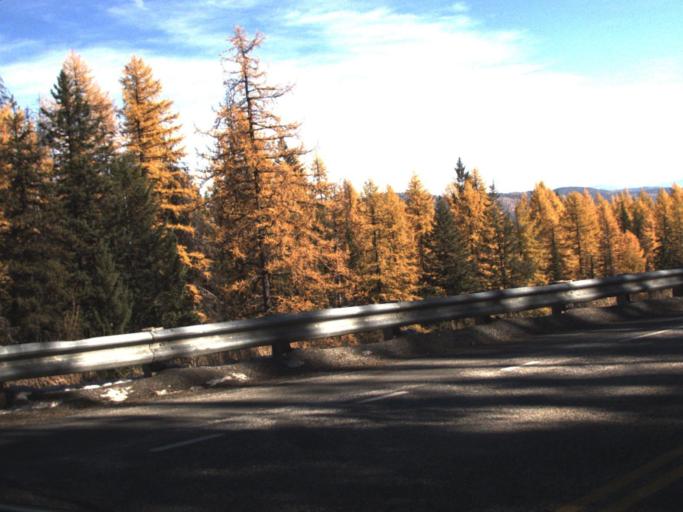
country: US
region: Washington
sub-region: Ferry County
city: Republic
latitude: 48.6071
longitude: -118.4772
